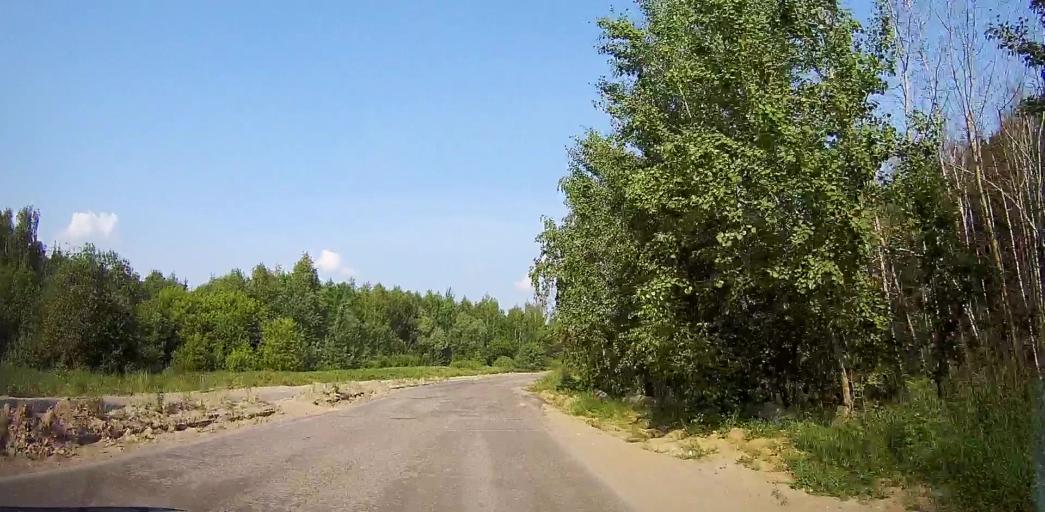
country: RU
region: Moskovskaya
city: Yakovlevskoye
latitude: 55.4313
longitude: 37.8897
